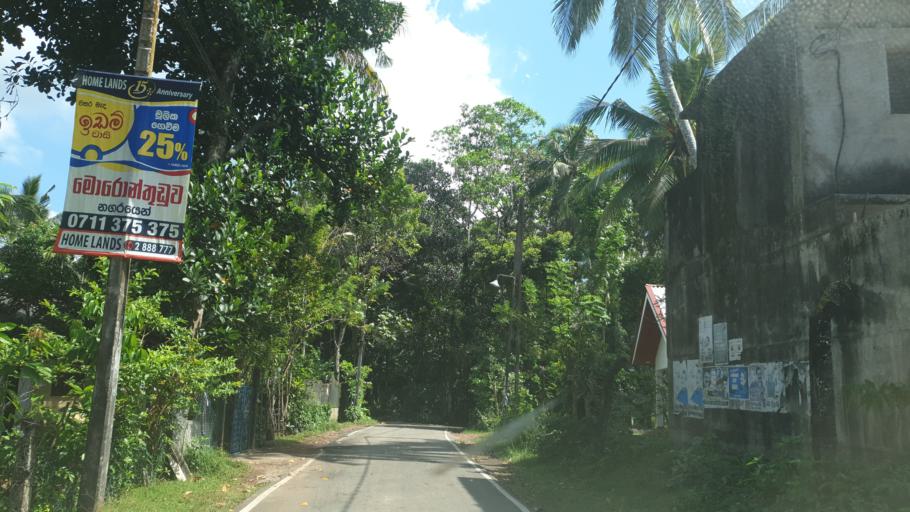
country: LK
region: Western
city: Panadura
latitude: 6.6835
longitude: 79.9440
